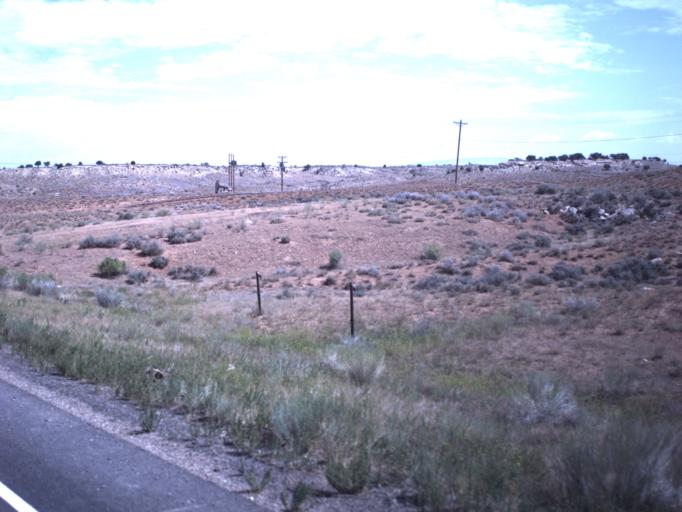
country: US
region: Utah
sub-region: Uintah County
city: Naples
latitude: 40.1875
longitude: -109.3309
